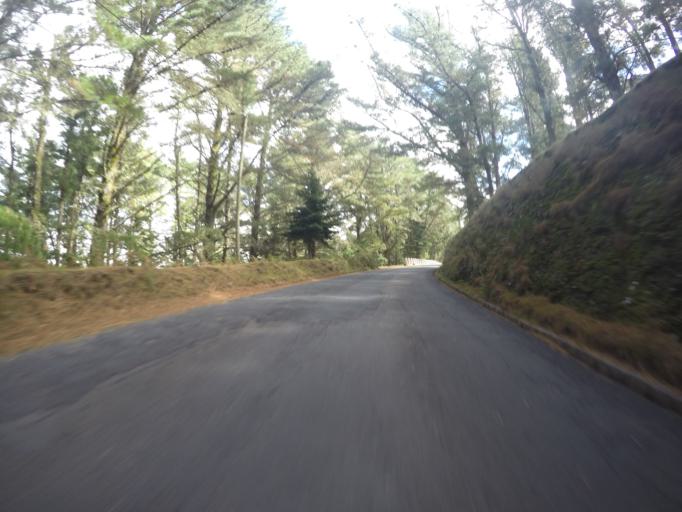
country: PT
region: Madeira
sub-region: Funchal
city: Nossa Senhora do Monte
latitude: 32.6962
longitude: -16.8789
